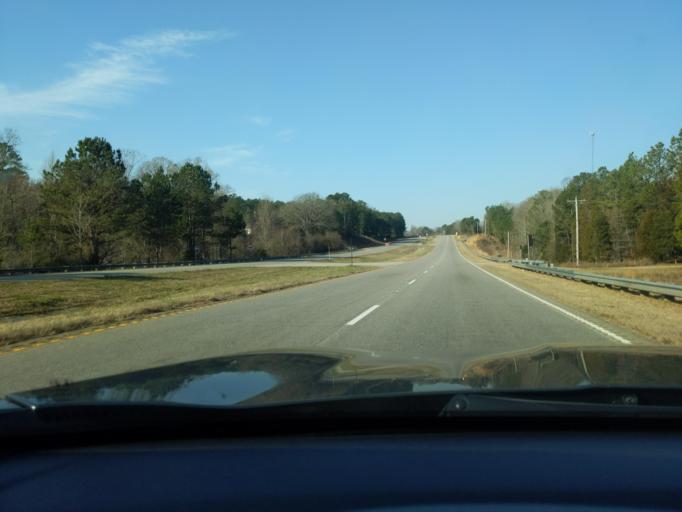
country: US
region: South Carolina
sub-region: Greenwood County
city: Greenwood
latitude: 34.1894
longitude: -82.2657
